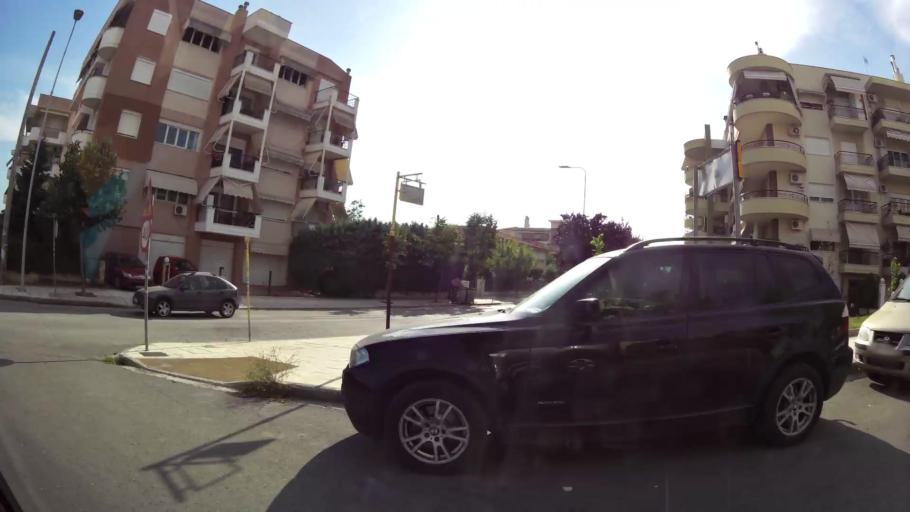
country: GR
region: Central Macedonia
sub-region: Nomos Thessalonikis
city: Kalamaria
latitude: 40.5701
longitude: 22.9669
